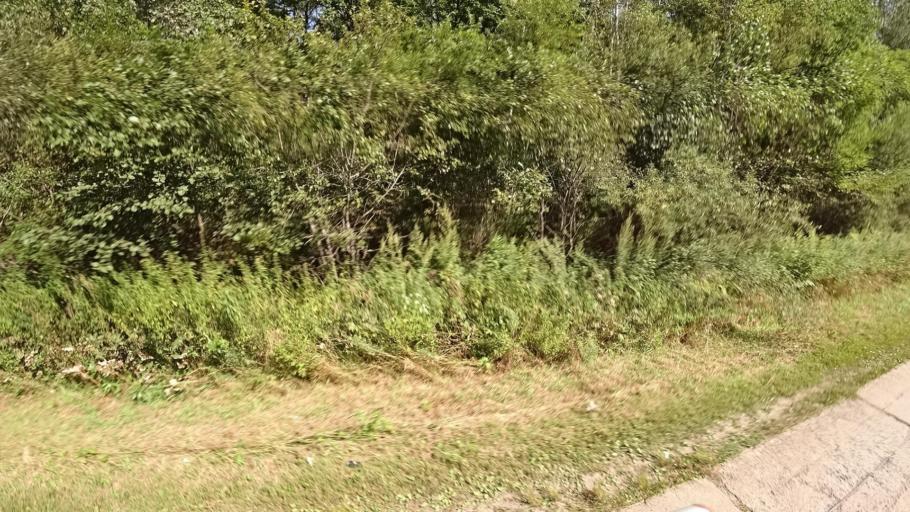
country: RU
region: Khabarovsk Krai
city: Khor
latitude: 47.9854
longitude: 135.0966
